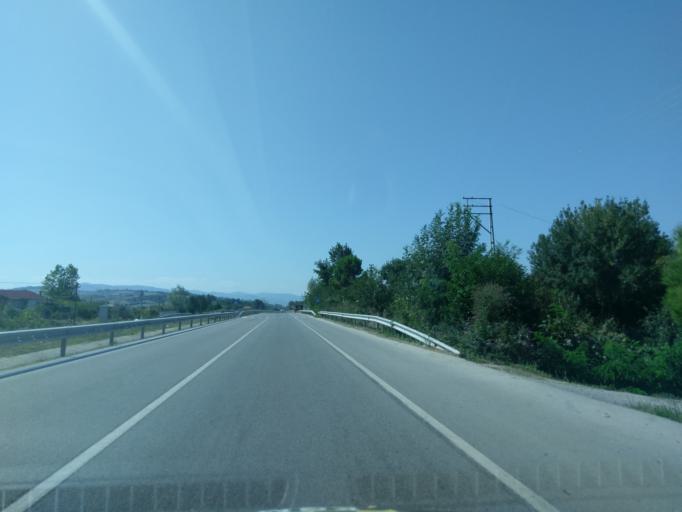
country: TR
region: Samsun
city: Alacam
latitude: 41.6091
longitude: 35.6604
